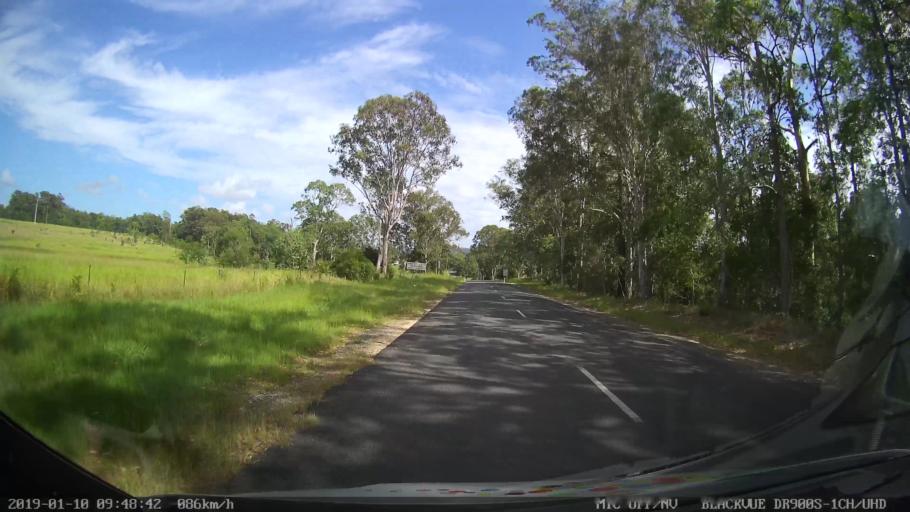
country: AU
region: New South Wales
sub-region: Coffs Harbour
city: Nana Glen
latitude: -30.0696
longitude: 152.9853
